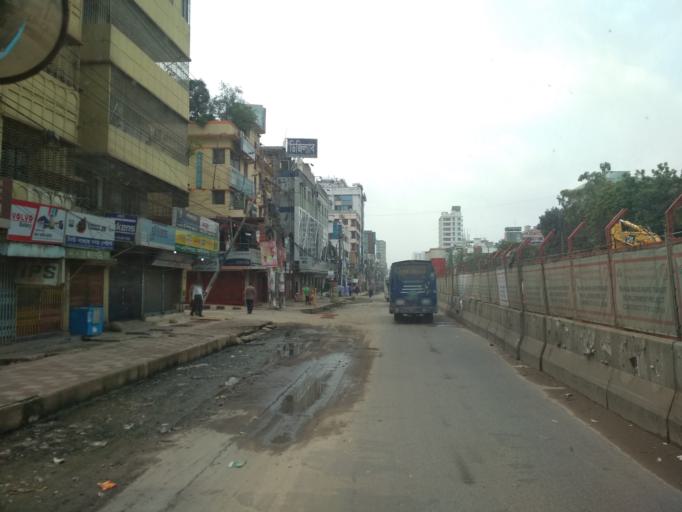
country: BD
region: Dhaka
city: Azimpur
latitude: 23.8122
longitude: 90.3673
